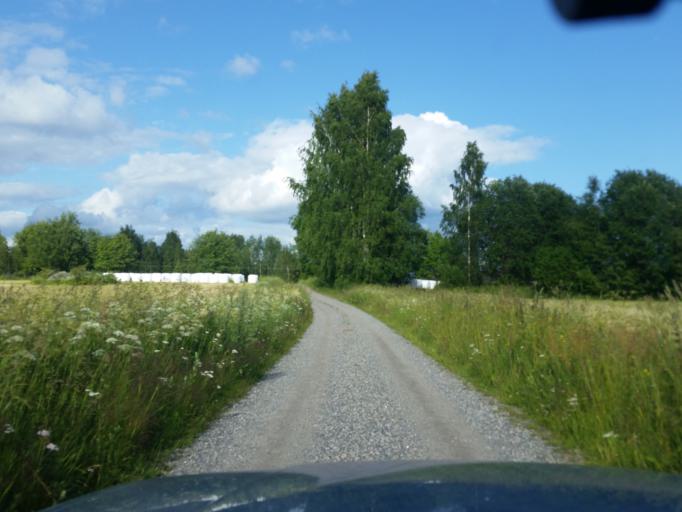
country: FI
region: Southern Savonia
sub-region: Savonlinna
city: Sulkava
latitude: 61.6784
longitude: 28.2856
